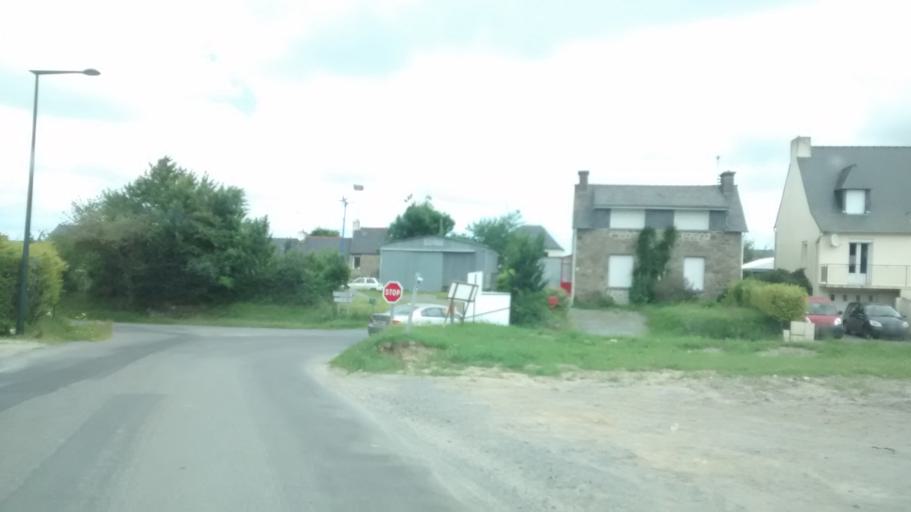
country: FR
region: Brittany
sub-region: Departement d'Ille-et-Vilaine
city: Saint-Meloir-des-Ondes
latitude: 48.6406
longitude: -1.9121
